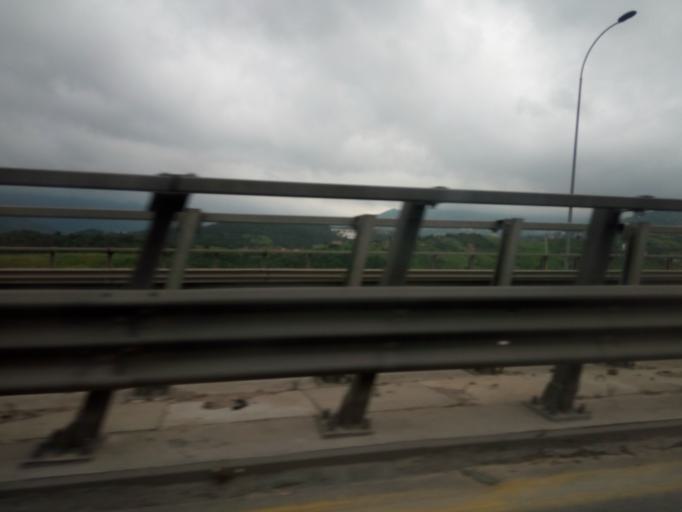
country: DZ
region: Bouira
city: Lakhdaria
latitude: 36.5846
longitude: 3.5381
